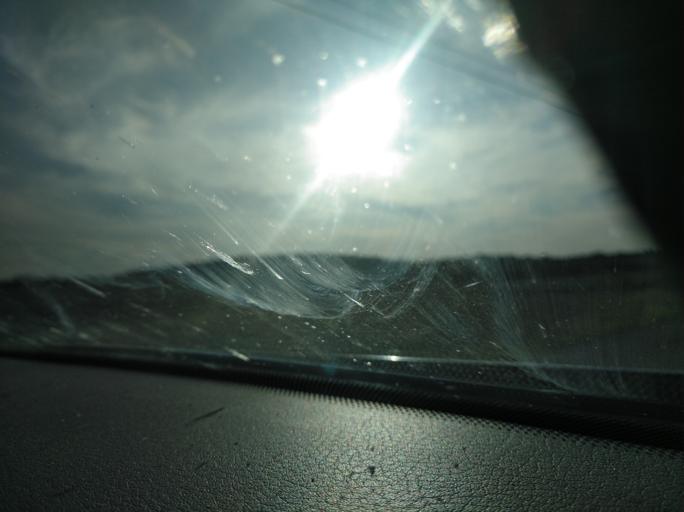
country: PT
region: Evora
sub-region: Estremoz
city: Estremoz
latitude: 38.9481
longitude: -7.4908
